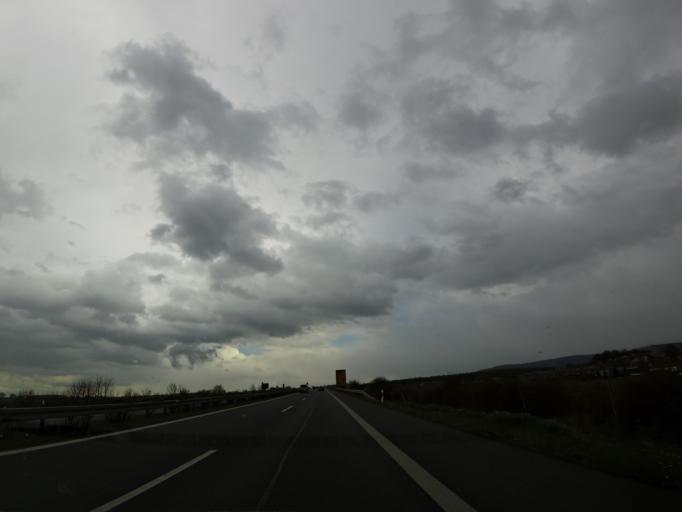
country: DE
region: Saxony-Anhalt
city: Stapelburg
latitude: 51.9115
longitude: 10.6698
